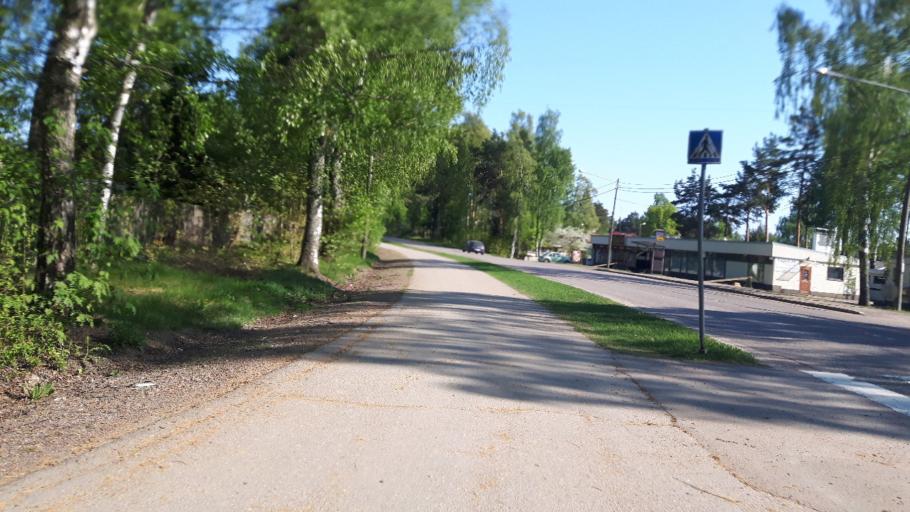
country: FI
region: Kymenlaakso
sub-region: Kotka-Hamina
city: Kotka
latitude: 60.4775
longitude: 26.8678
